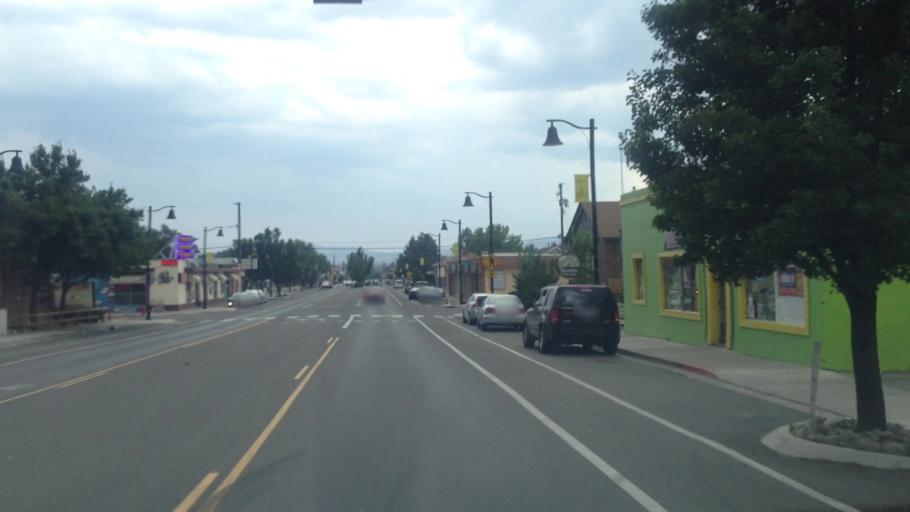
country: US
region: Nevada
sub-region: Washoe County
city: Reno
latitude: 39.5180
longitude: -119.8033
